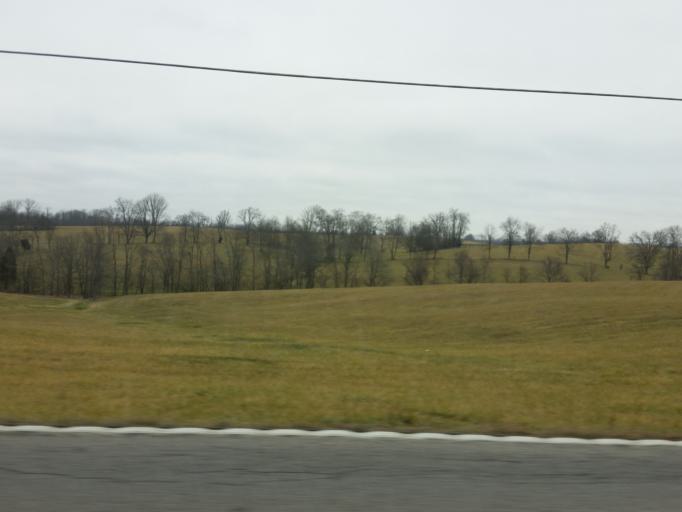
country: US
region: Kentucky
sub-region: Trimble County
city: Providence
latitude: 38.5208
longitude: -85.2256
